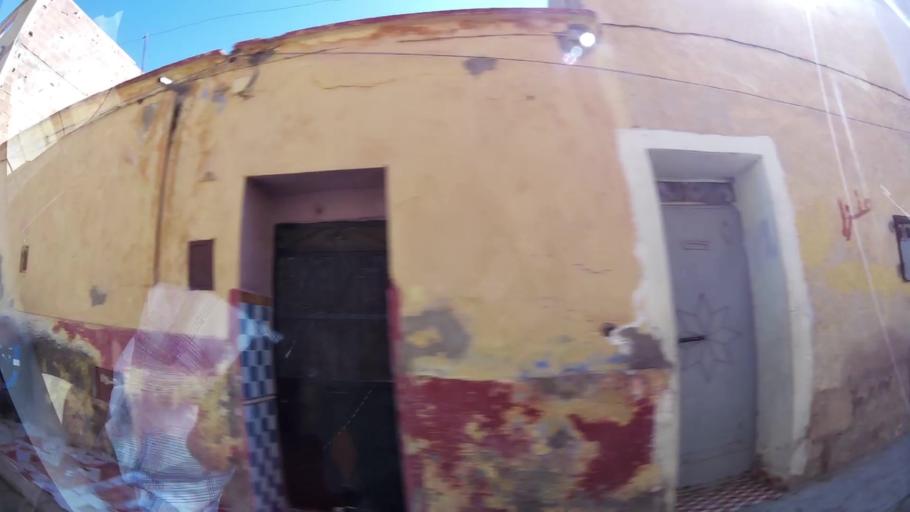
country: MA
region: Oriental
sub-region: Oujda-Angad
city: Oujda
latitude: 34.6809
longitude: -1.9274
